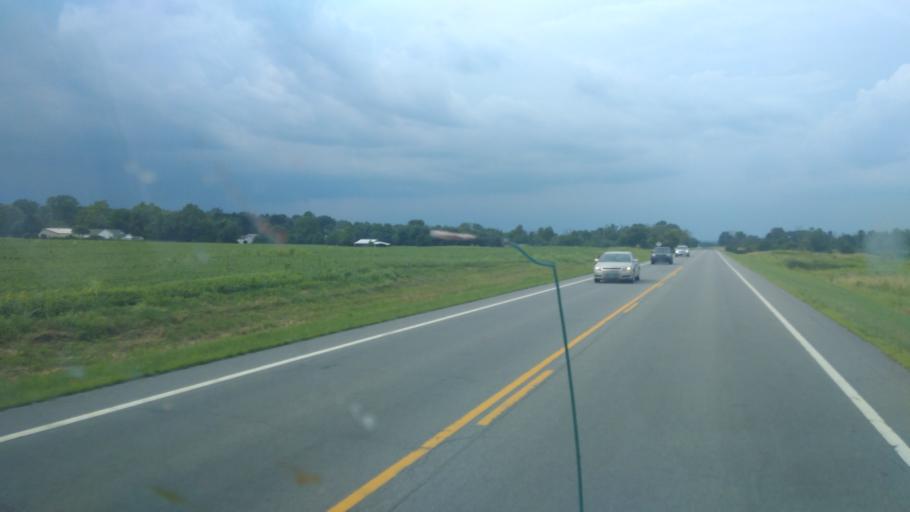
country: US
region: Ohio
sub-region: Fairfield County
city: Baltimore
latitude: 39.7830
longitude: -82.5736
